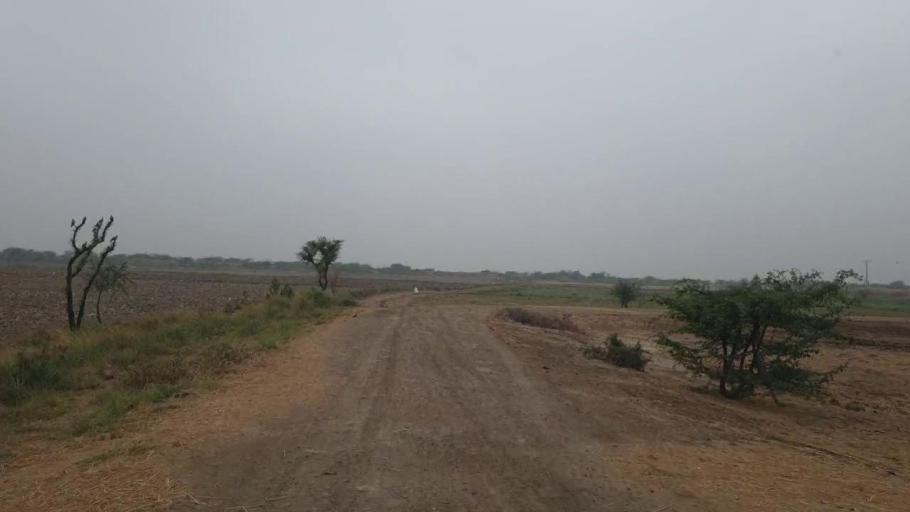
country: PK
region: Sindh
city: Badin
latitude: 24.6001
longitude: 68.6589
